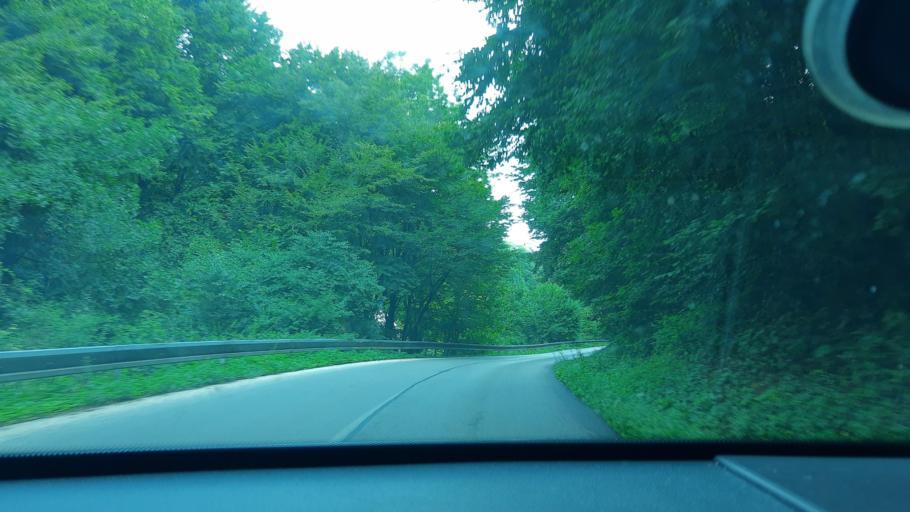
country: SK
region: Trnavsky
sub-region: Okres Trnava
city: Piestany
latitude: 48.6461
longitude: 17.9383
